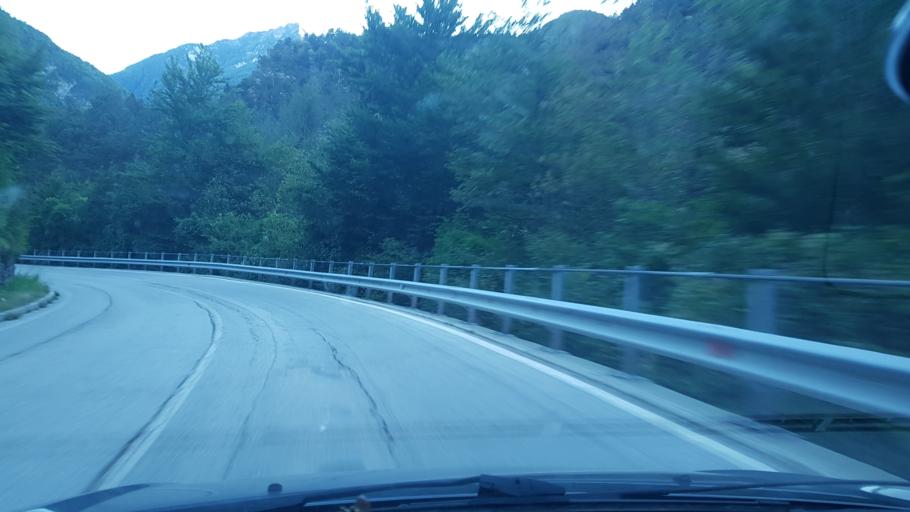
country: IT
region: Veneto
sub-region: Provincia di Belluno
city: Forno di Zoldo
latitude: 46.3253
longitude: 12.2321
